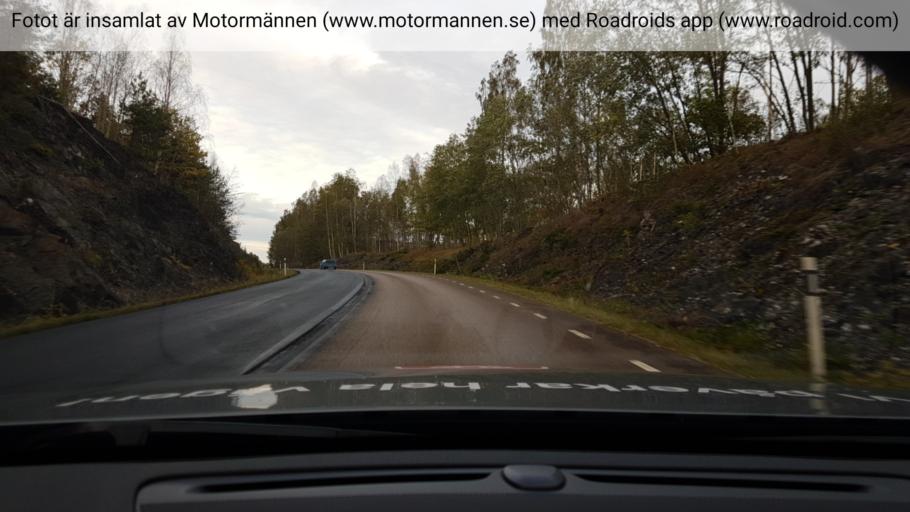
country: SE
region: Vaestra Goetaland
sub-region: Bengtsfors Kommun
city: Dals Langed
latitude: 59.0509
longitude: 12.4787
